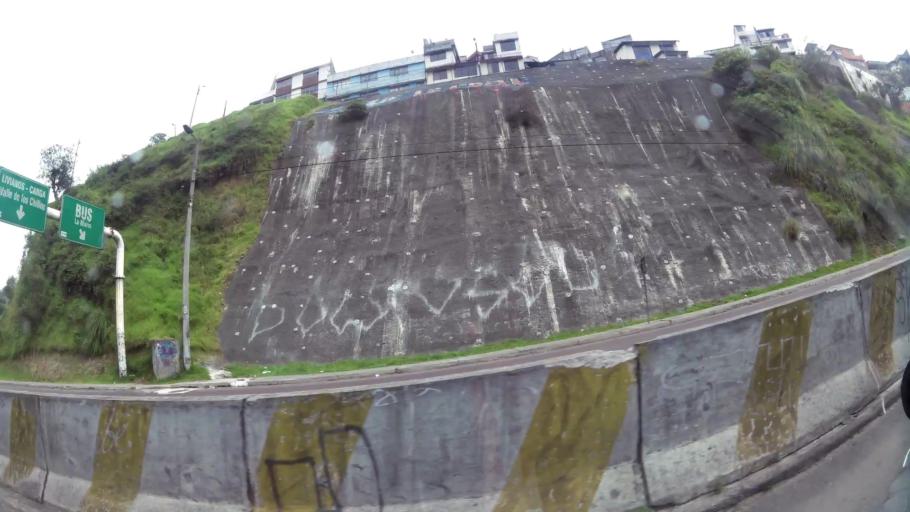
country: EC
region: Pichincha
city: Quito
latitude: -0.2315
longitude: -78.5024
